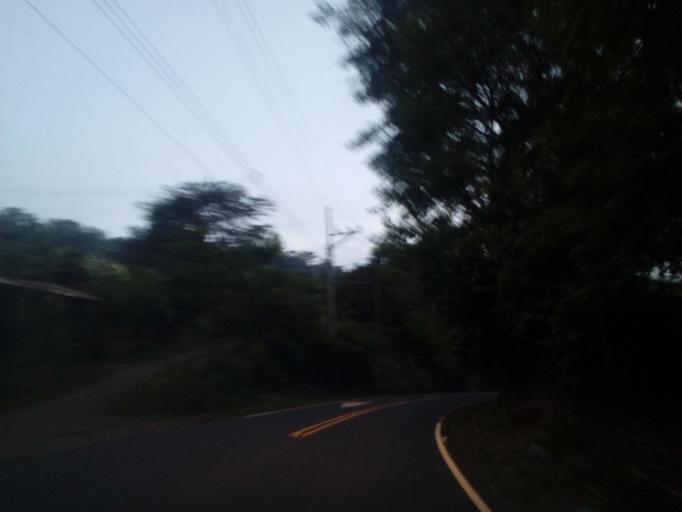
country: CR
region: Guanacaste
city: Samara
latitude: 9.9725
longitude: -85.5081
